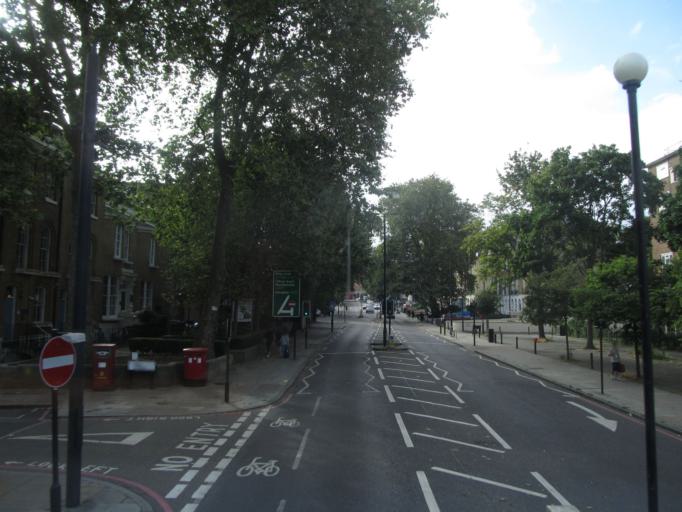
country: GB
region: England
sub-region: Greater London
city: Islington
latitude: 51.5305
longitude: -0.1006
